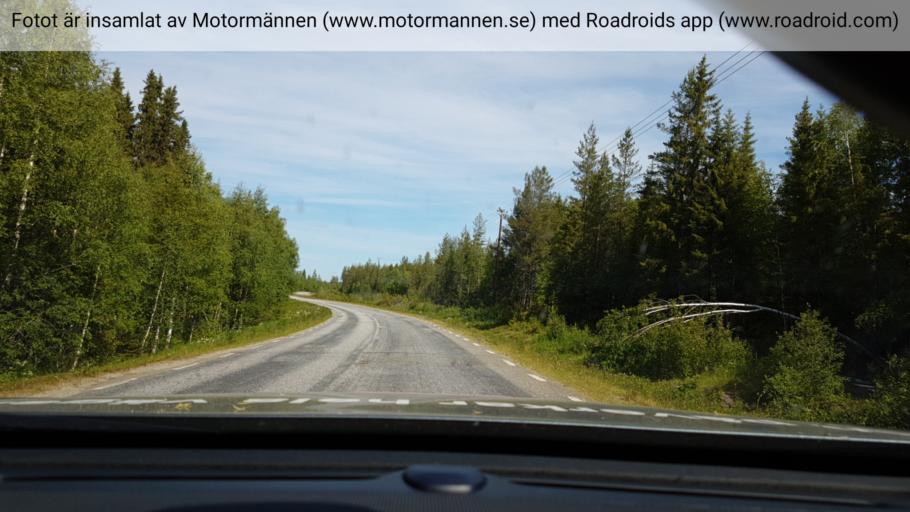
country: SE
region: Vaesterbotten
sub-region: Vilhelmina Kommun
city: Sjoberg
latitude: 64.4934
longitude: 15.9383
